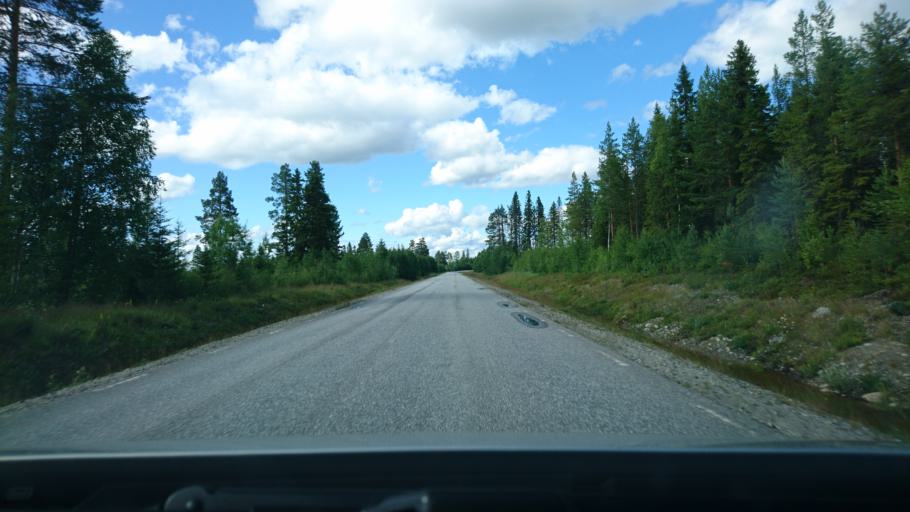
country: SE
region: Vaesterbotten
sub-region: Asele Kommun
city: Asele
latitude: 64.0535
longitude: 17.2803
